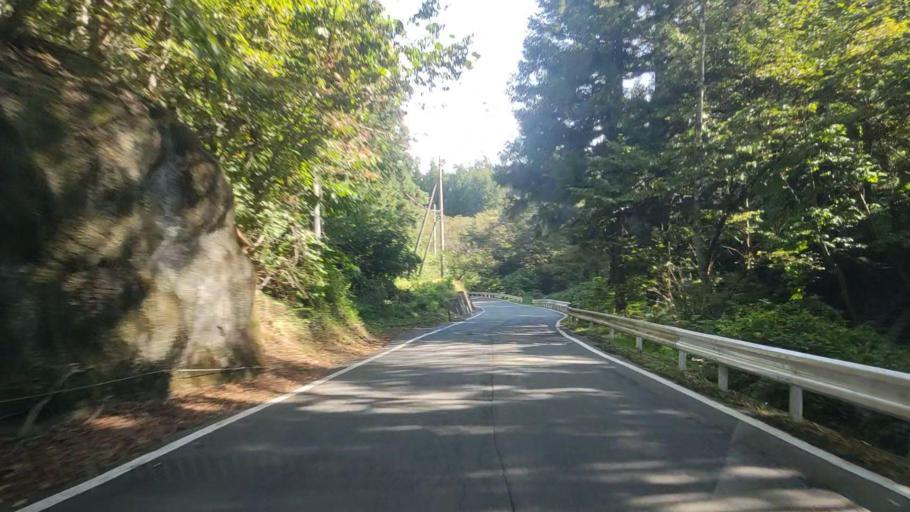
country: JP
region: Gunma
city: Nakanojomachi
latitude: 36.6008
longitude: 138.7120
